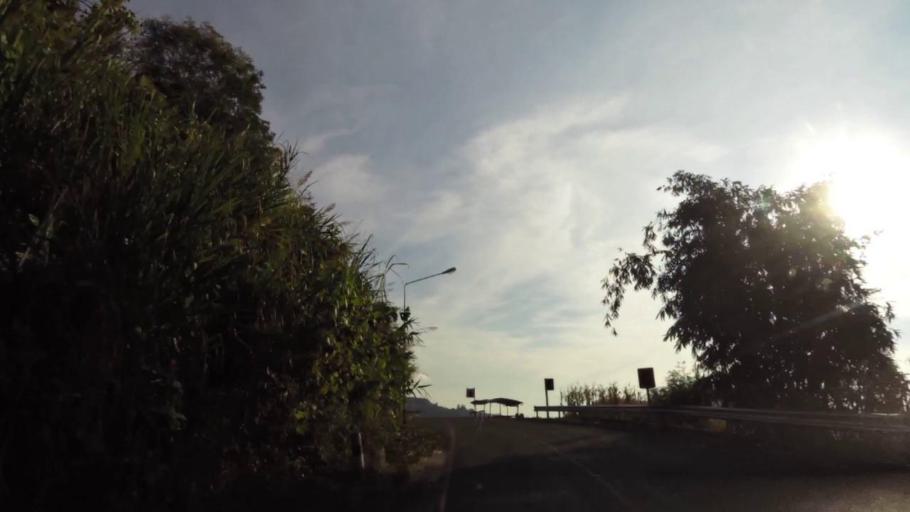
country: TH
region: Chiang Rai
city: Khun Tan
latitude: 19.8518
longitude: 100.4367
